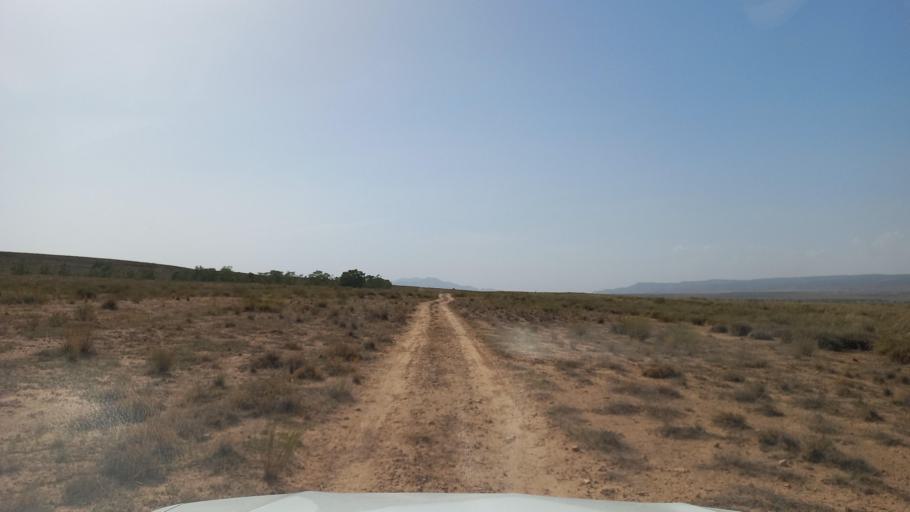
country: TN
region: Al Qasrayn
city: Kasserine
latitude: 35.2142
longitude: 8.9991
